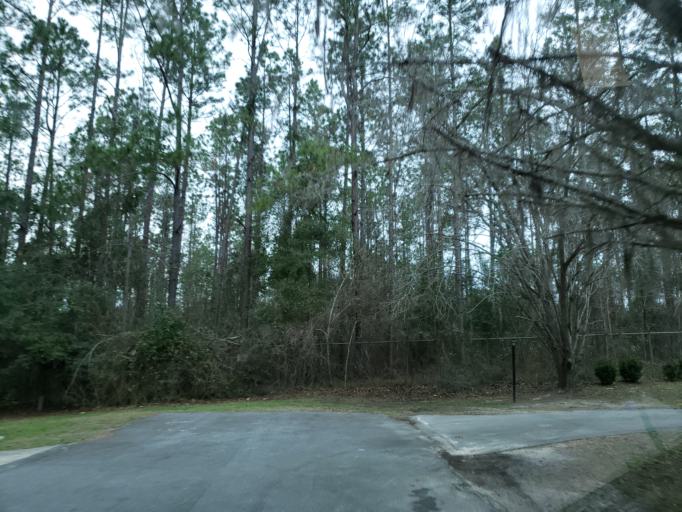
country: US
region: Georgia
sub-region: Lowndes County
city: Remerton
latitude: 30.8994
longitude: -83.3646
